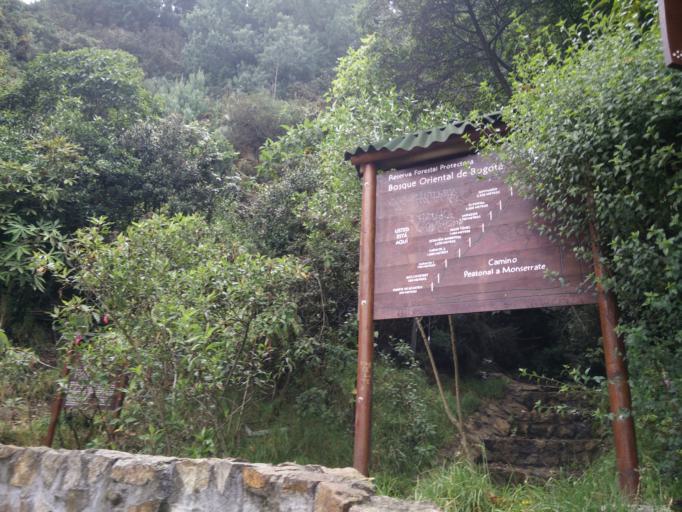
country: CO
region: Bogota D.C.
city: Bogota
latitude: 4.6074
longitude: -74.0593
